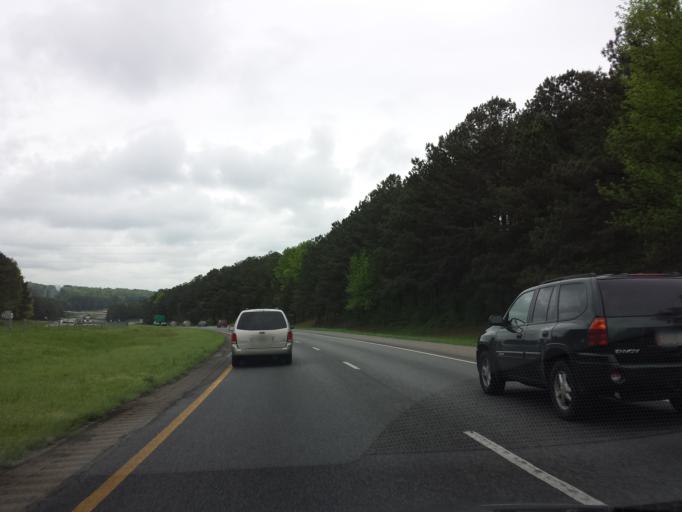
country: US
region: Georgia
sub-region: Cherokee County
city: Holly Springs
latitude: 34.1800
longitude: -84.5075
